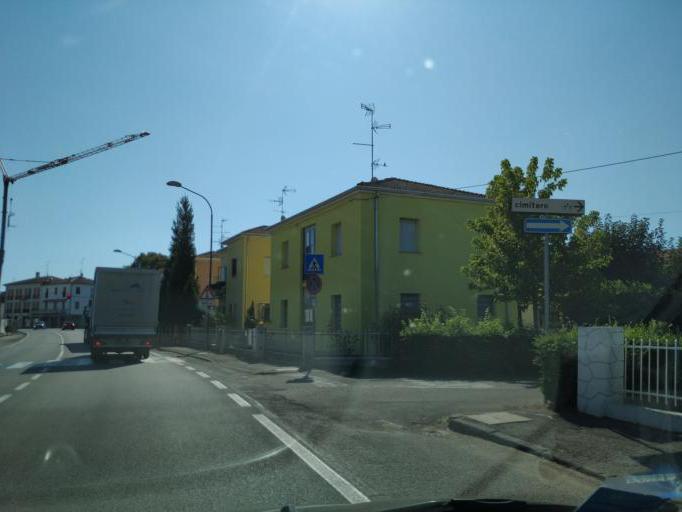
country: IT
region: Emilia-Romagna
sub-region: Provincia di Ferrara
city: Dosso
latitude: 44.7679
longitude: 11.3336
